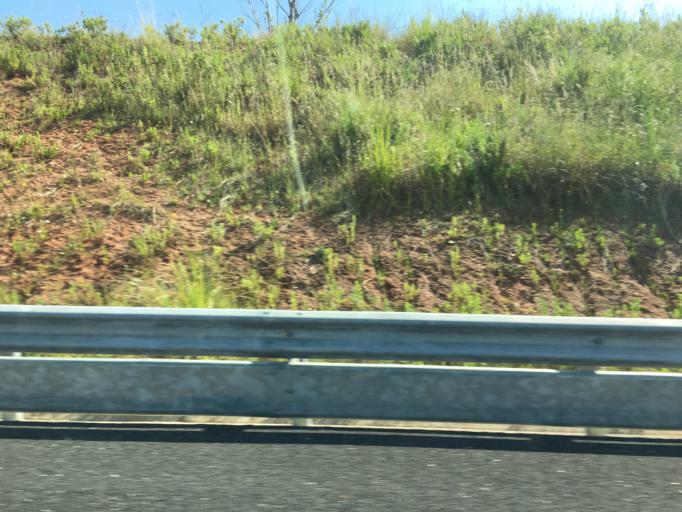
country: PT
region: Lisbon
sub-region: Odivelas
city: Pontinha
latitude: 38.7640
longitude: -9.2030
